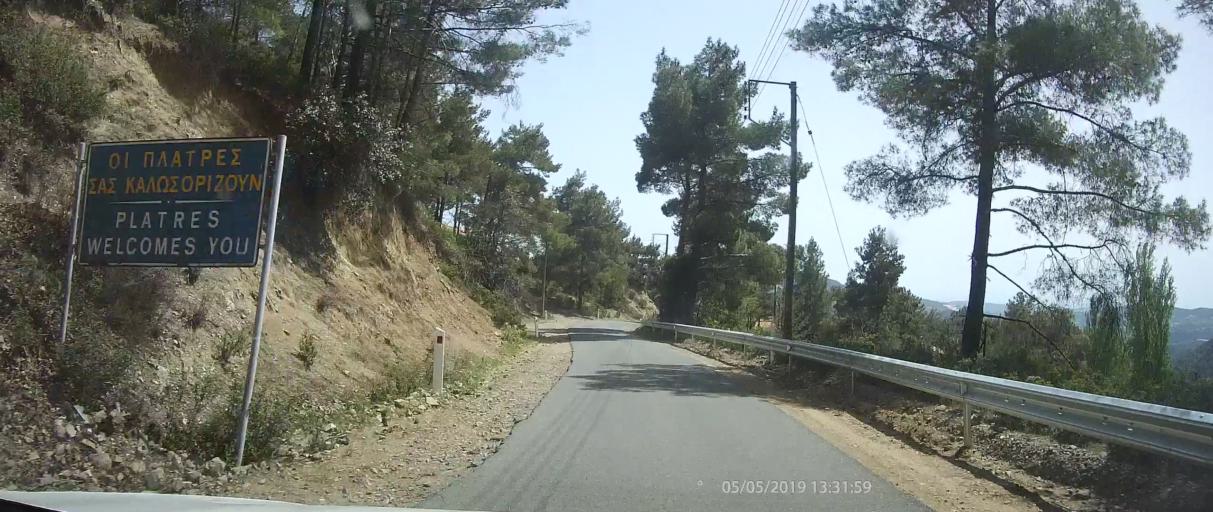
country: CY
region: Lefkosia
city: Kakopetria
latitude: 34.8910
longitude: 32.8517
